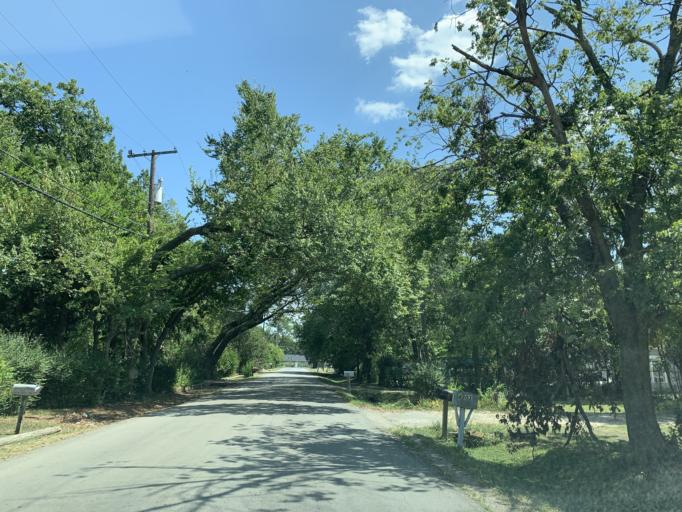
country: US
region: Texas
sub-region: Dallas County
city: Dallas
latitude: 32.7127
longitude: -96.7655
